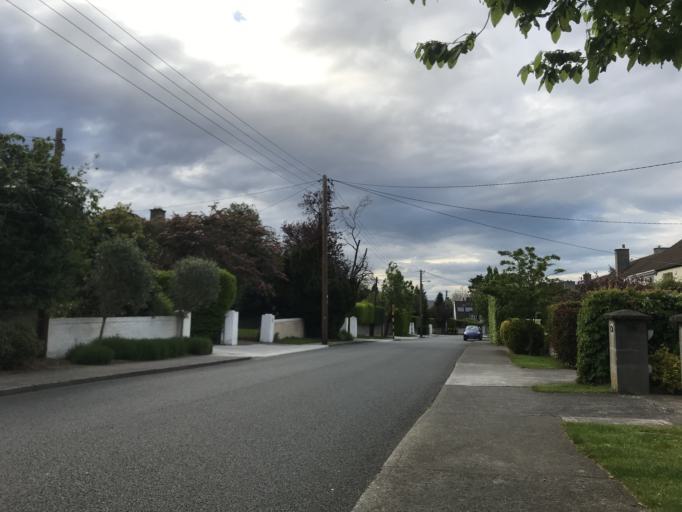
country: IE
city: Booterstown
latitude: 53.2953
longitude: -6.1975
